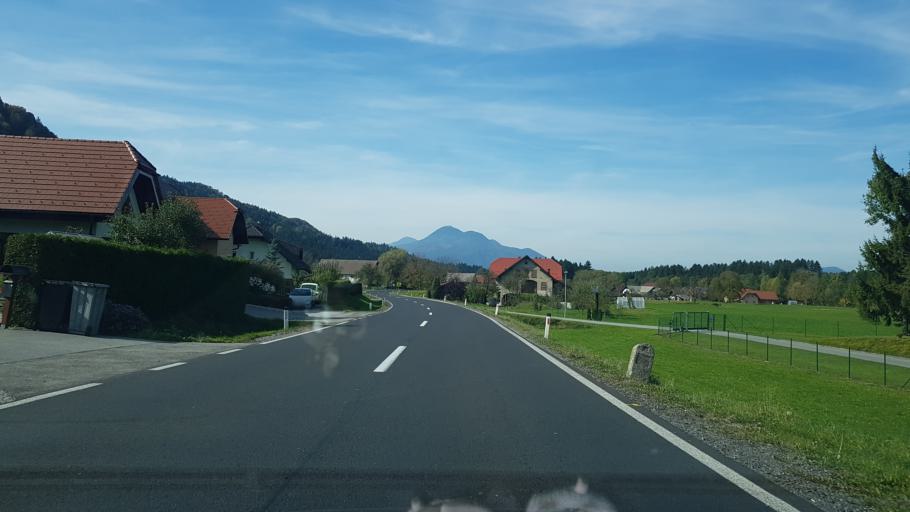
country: SI
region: Slovenj Gradec
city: Legen
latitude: 46.4464
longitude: 15.1782
